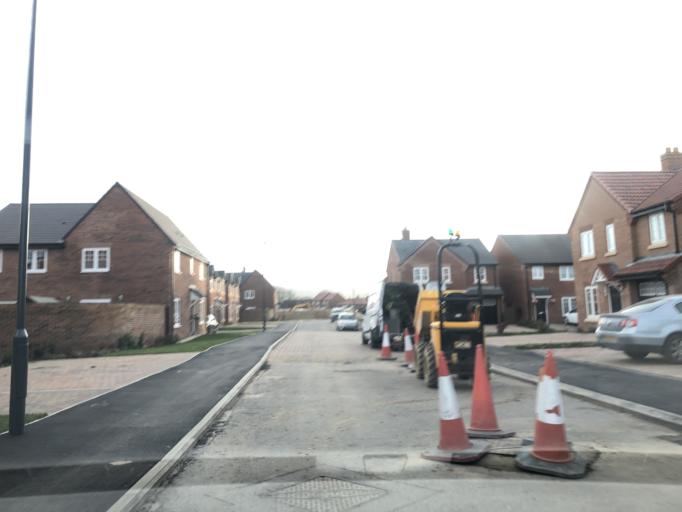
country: GB
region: England
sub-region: North Yorkshire
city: Stokesley
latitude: 54.4704
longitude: -1.2033
